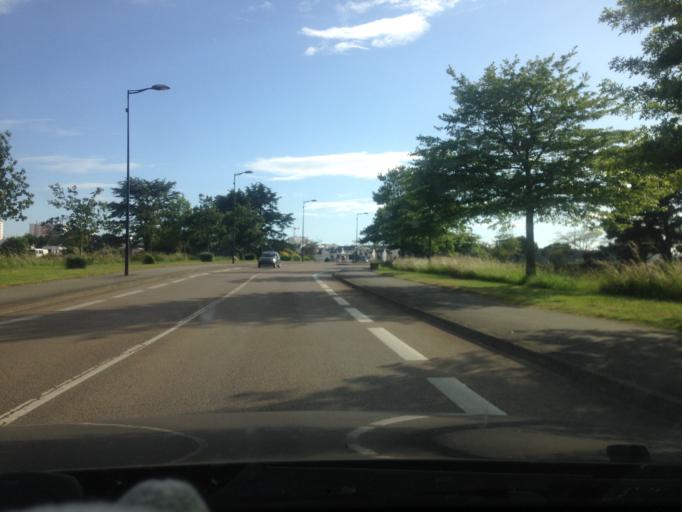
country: FR
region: Brittany
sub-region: Departement du Morbihan
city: Lanester
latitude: 47.7614
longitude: -3.3522
